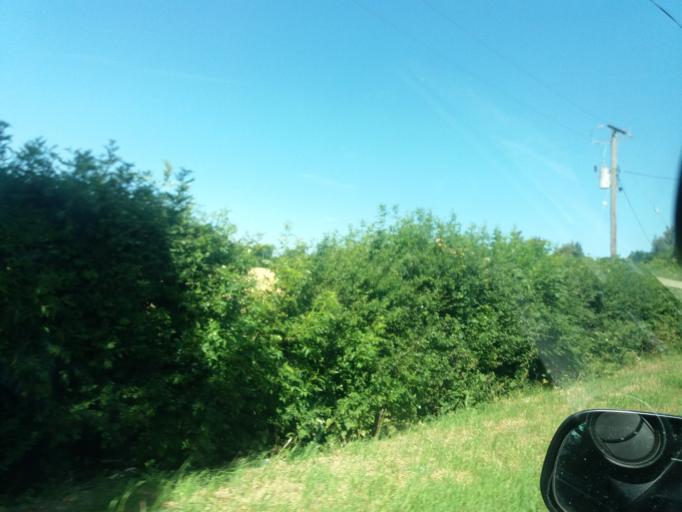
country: IE
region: Leinster
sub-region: Fingal County
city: Swords
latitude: 53.4643
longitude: -6.2721
